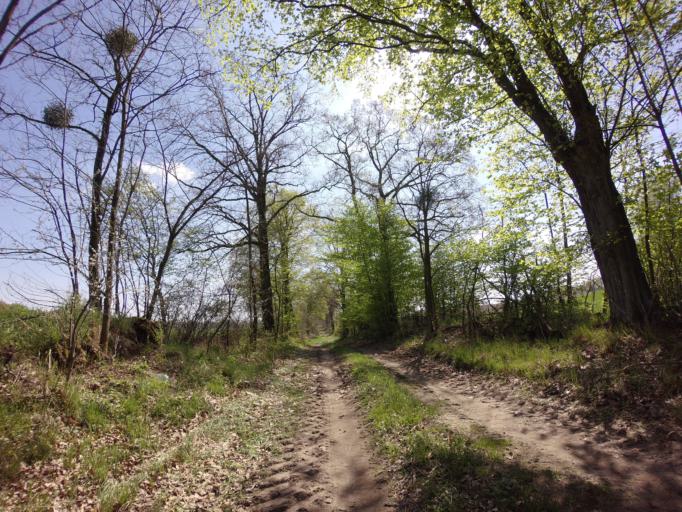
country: PL
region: West Pomeranian Voivodeship
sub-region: Powiat stargardzki
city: Suchan
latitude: 53.2002
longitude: 15.3076
